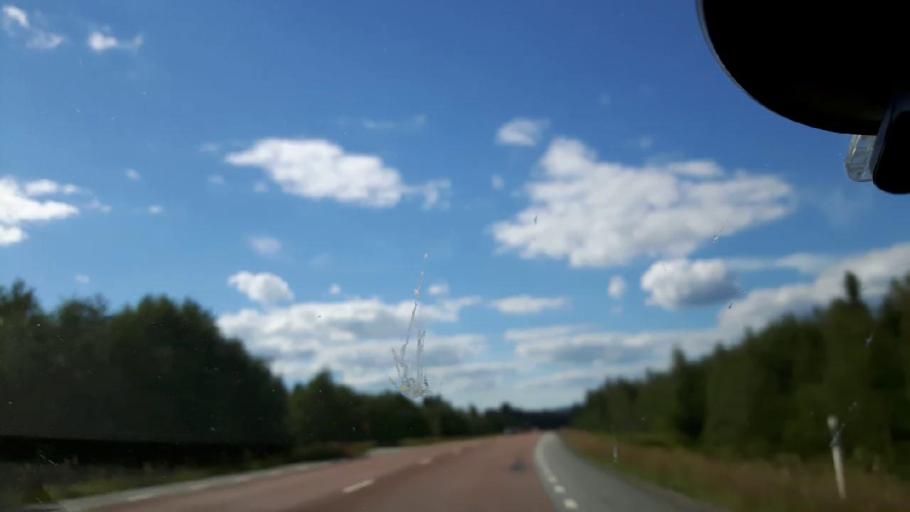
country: SE
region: Jaemtland
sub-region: Braecke Kommun
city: Braecke
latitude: 62.8164
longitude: 15.3438
